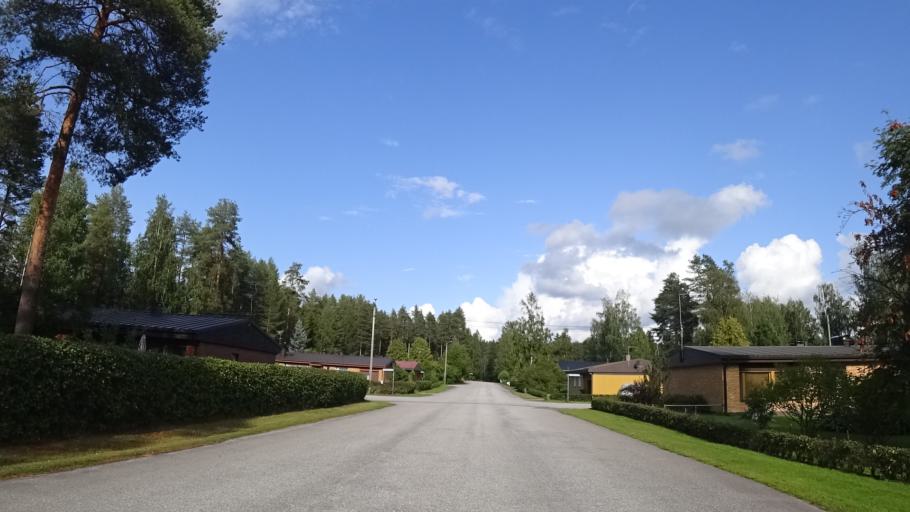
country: FI
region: North Karelia
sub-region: Pielisen Karjala
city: Lieksa
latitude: 63.3343
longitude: 30.0296
